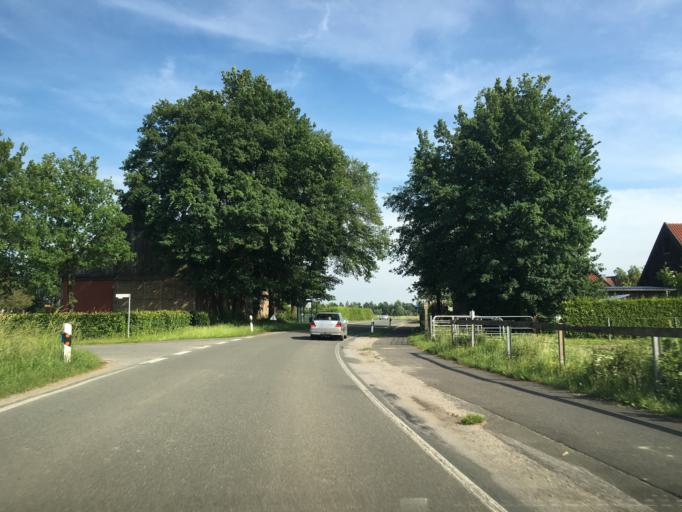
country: DE
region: North Rhine-Westphalia
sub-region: Regierungsbezirk Munster
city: Nordwalde
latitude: 52.1157
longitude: 7.4554
